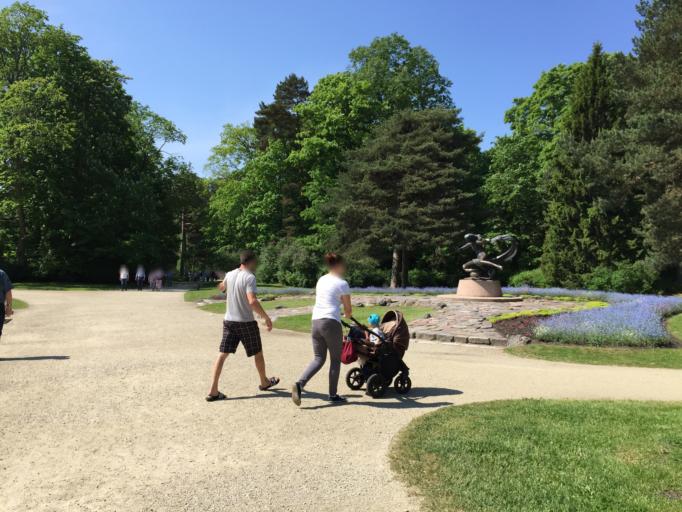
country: LT
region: Klaipedos apskritis
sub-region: Klaipeda
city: Palanga
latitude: 55.9098
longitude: 21.0607
